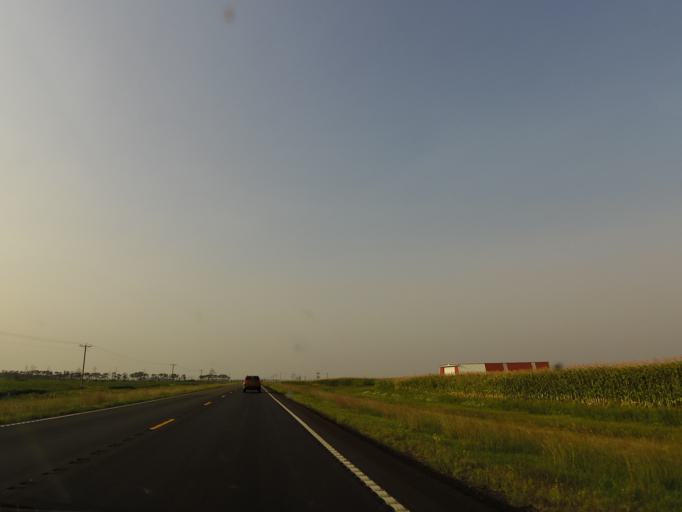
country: US
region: North Dakota
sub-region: Traill County
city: Mayville
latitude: 47.4194
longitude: -97.3260
